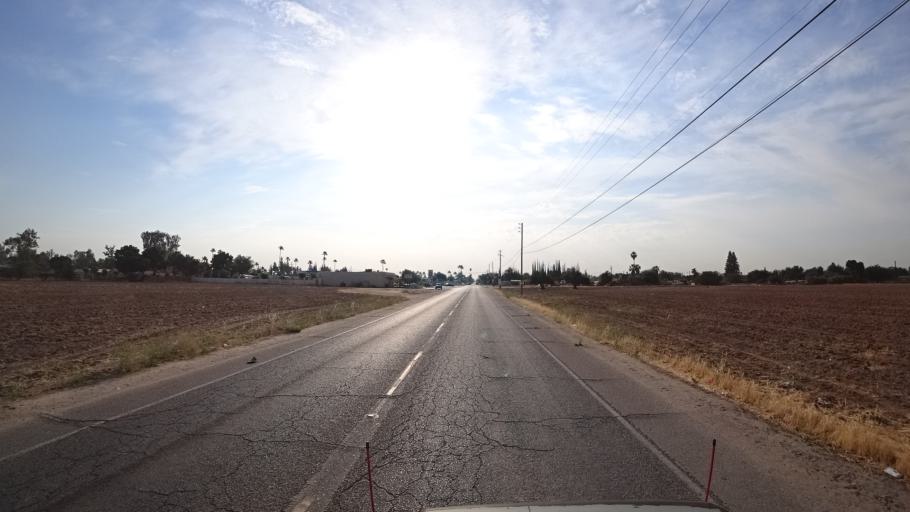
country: US
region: California
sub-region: Fresno County
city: West Park
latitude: 36.7574
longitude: -119.8463
